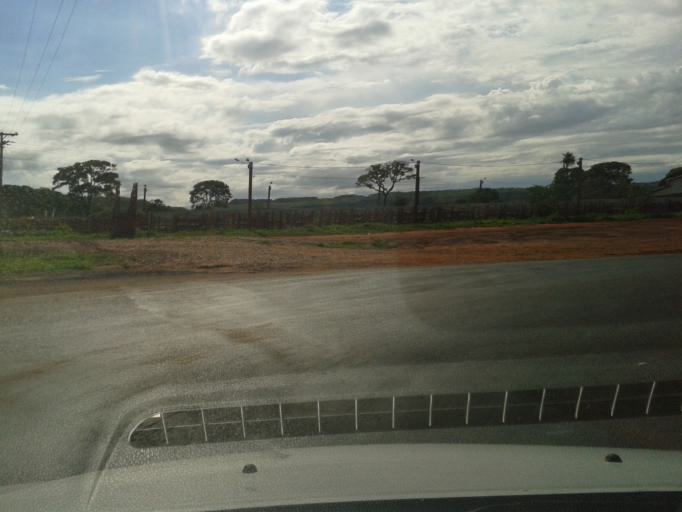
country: BR
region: Minas Gerais
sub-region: Ituiutaba
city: Ituiutaba
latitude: -19.2126
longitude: -49.7783
